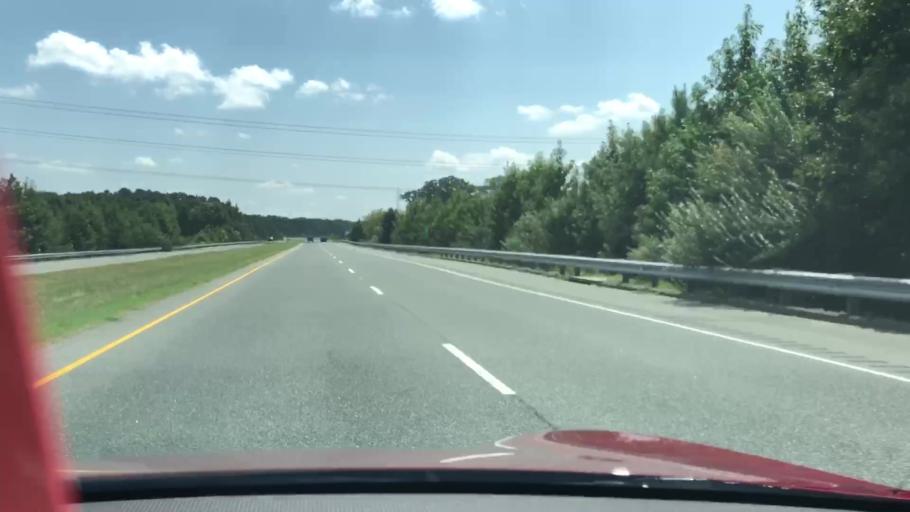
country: US
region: North Carolina
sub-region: Currituck County
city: Moyock
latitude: 36.6515
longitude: -76.2268
